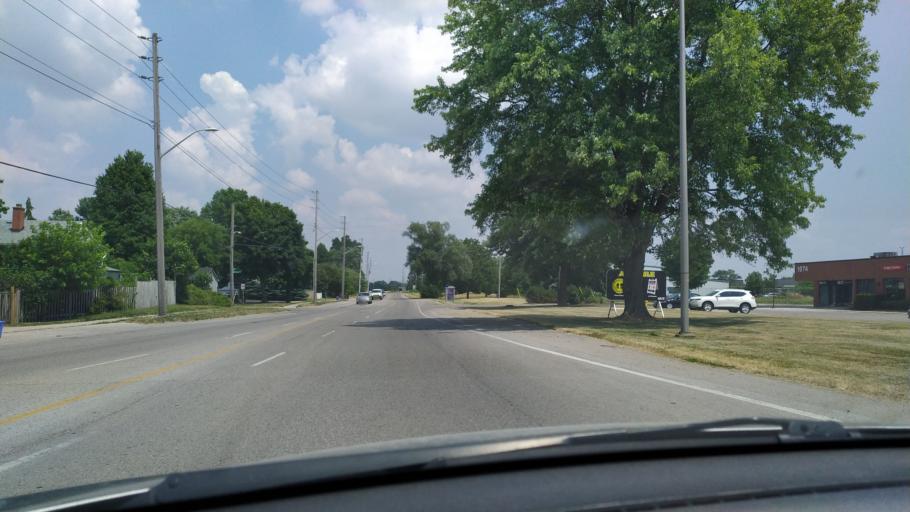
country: CA
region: Ontario
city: London
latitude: 42.9348
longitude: -81.2202
